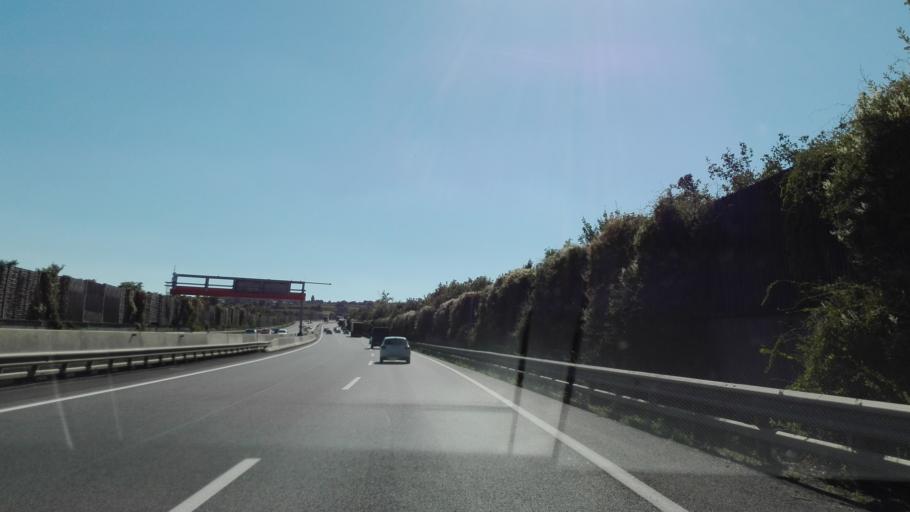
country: AT
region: Lower Austria
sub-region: Politischer Bezirk Modling
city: Brunn am Gebirge
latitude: 48.1146
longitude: 16.2793
